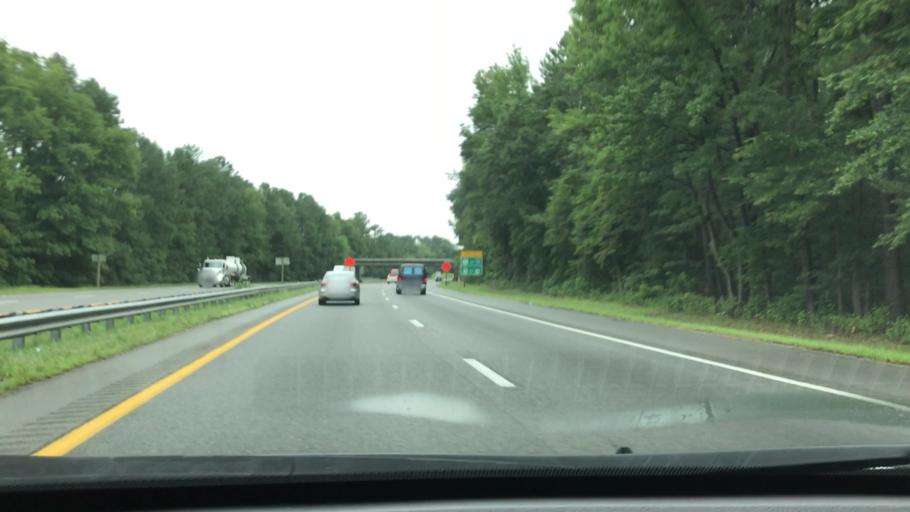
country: US
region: Virginia
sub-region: City of Emporia
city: Emporia
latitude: 36.6843
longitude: -77.5580
